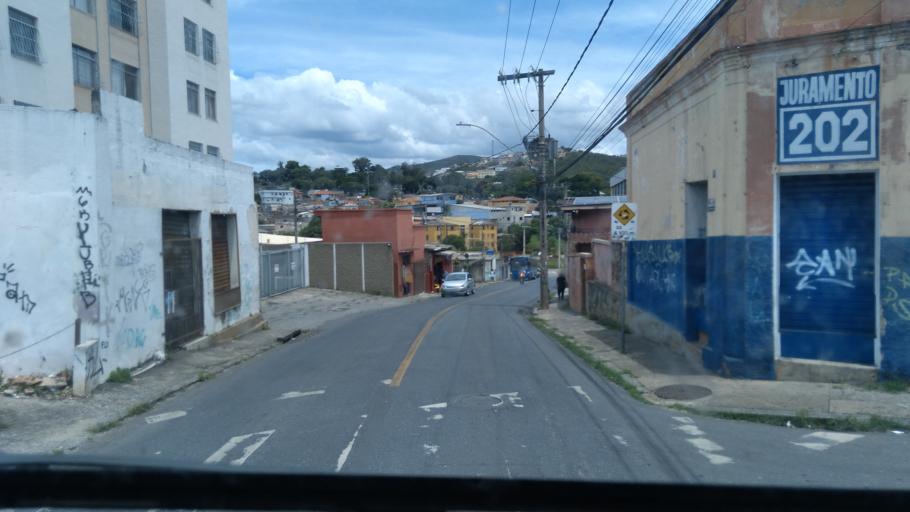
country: BR
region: Minas Gerais
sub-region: Belo Horizonte
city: Belo Horizonte
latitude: -19.9169
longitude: -43.9037
